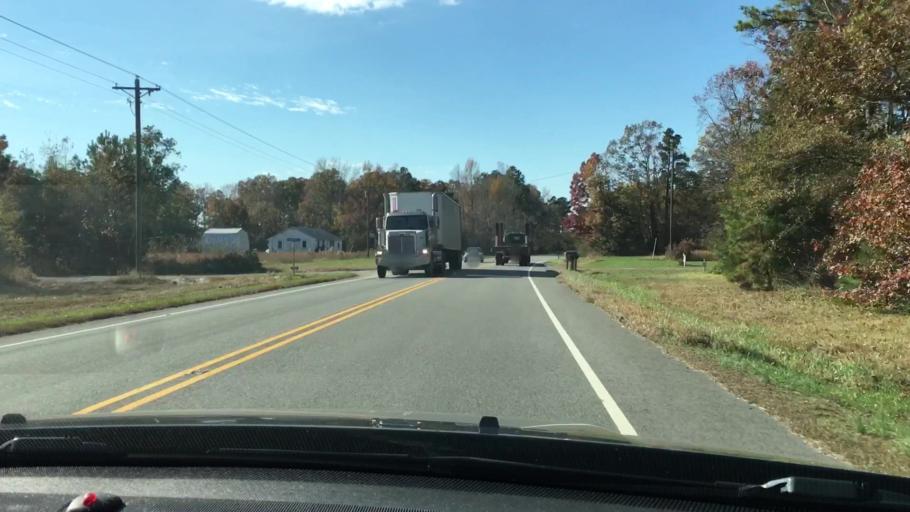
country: US
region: Virginia
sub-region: Hanover County
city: Hanover
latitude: 37.8115
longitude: -77.2871
